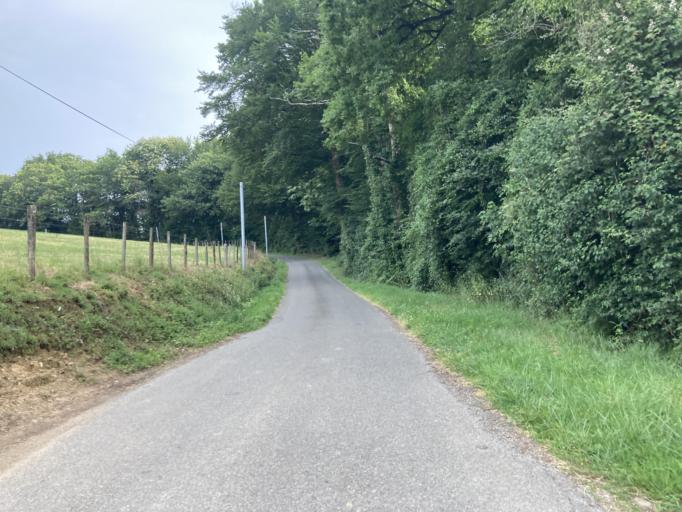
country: FR
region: Aquitaine
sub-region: Departement des Pyrenees-Atlantiques
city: Ledeuix
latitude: 43.2483
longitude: -0.6218
